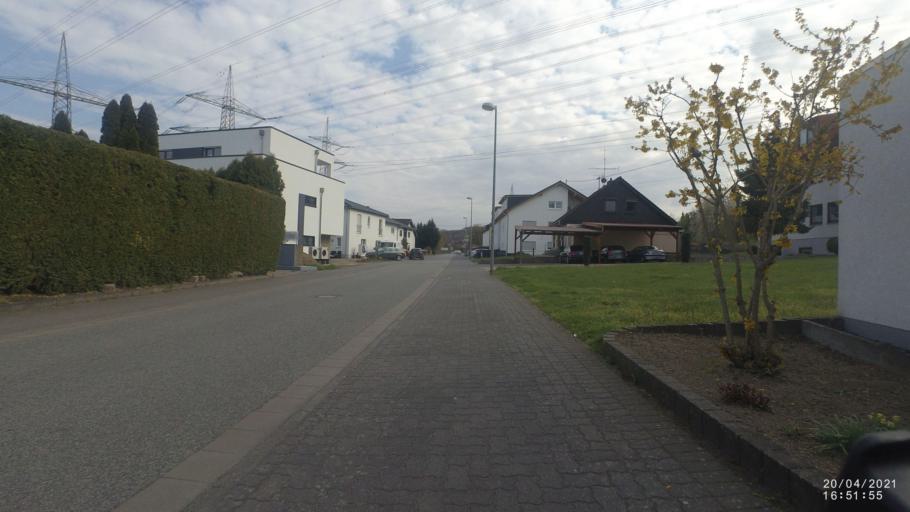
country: DE
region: Rheinland-Pfalz
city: Kettig
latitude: 50.4040
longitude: 7.4612
